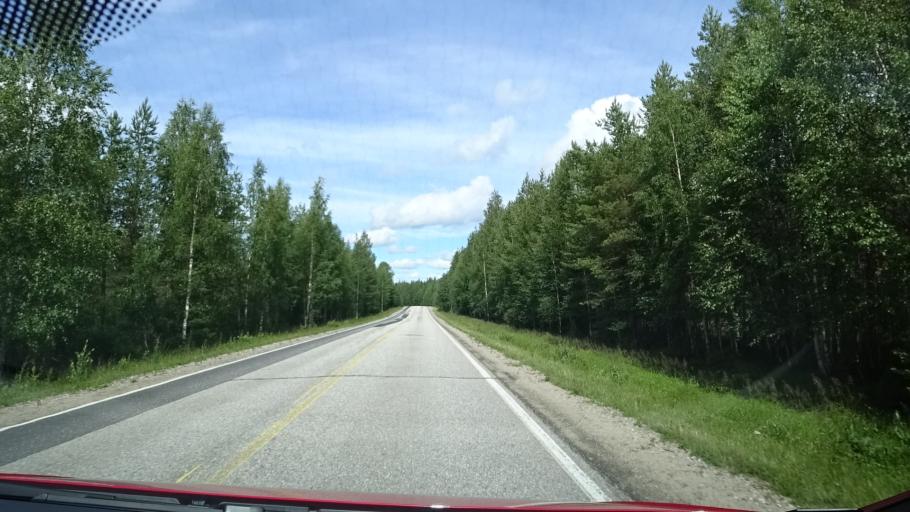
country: FI
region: Kainuu
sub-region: Kehys-Kainuu
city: Kuhmo
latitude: 64.4437
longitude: 29.7978
